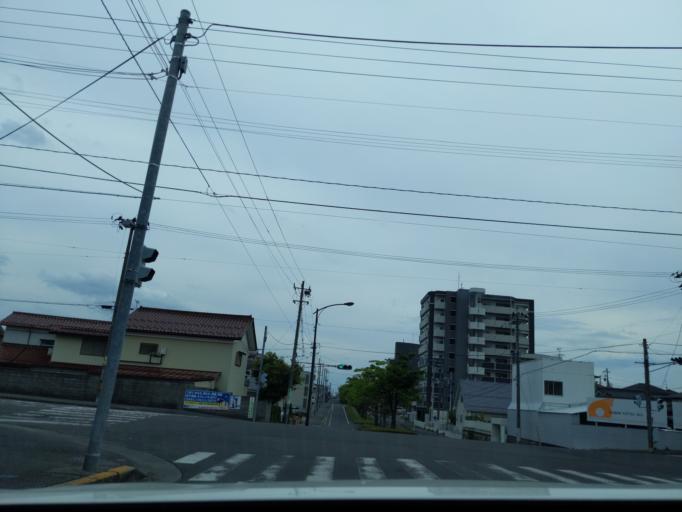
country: JP
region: Fukushima
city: Koriyama
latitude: 37.3908
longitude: 140.3646
